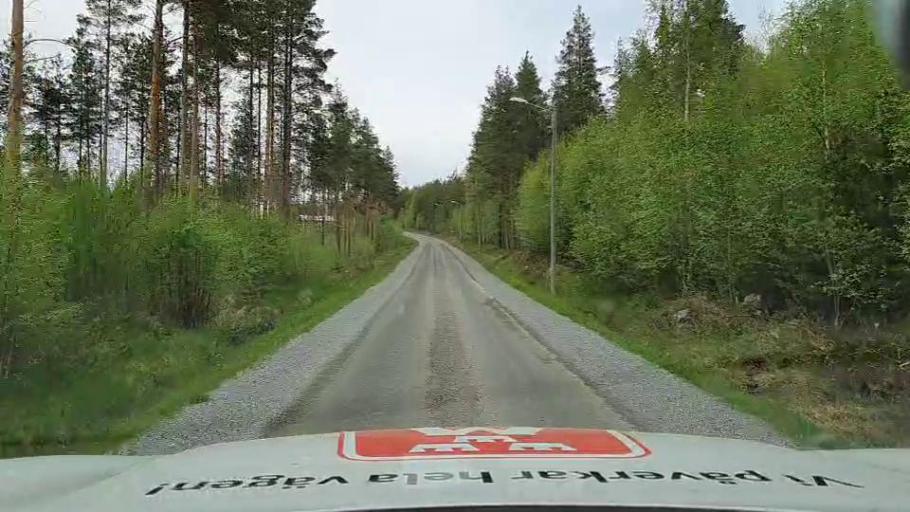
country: SE
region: Jaemtland
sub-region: Braecke Kommun
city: Braecke
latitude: 62.4604
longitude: 14.9182
